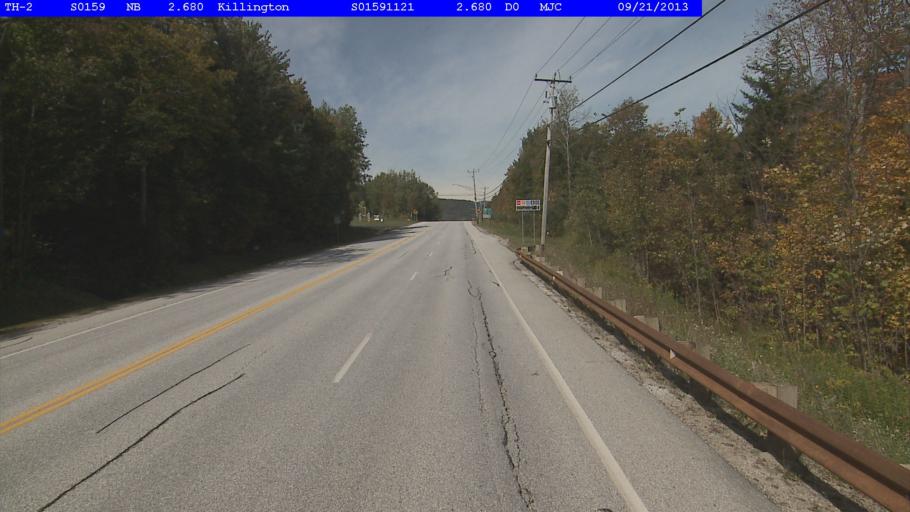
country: US
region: Vermont
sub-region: Rutland County
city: Rutland
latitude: 43.6644
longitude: -72.8005
